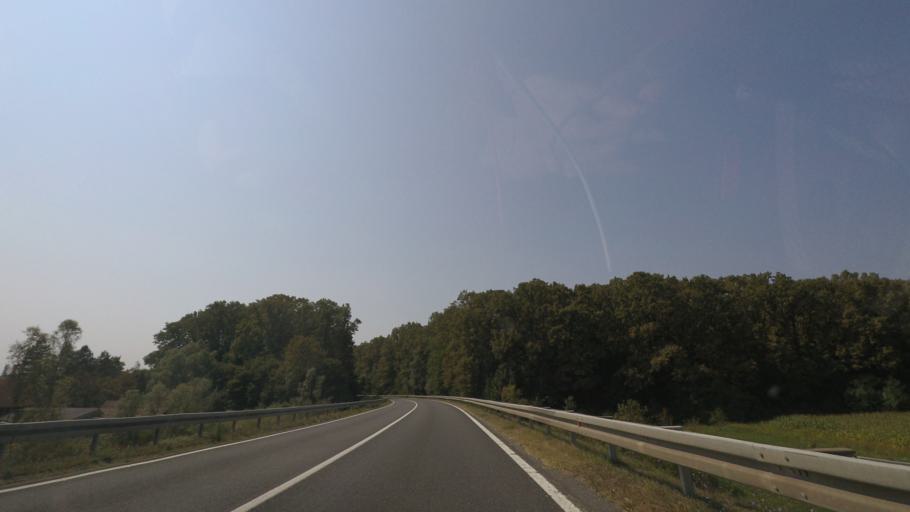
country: HR
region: Sisacko-Moslavacka
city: Novska
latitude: 45.3350
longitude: 16.9526
